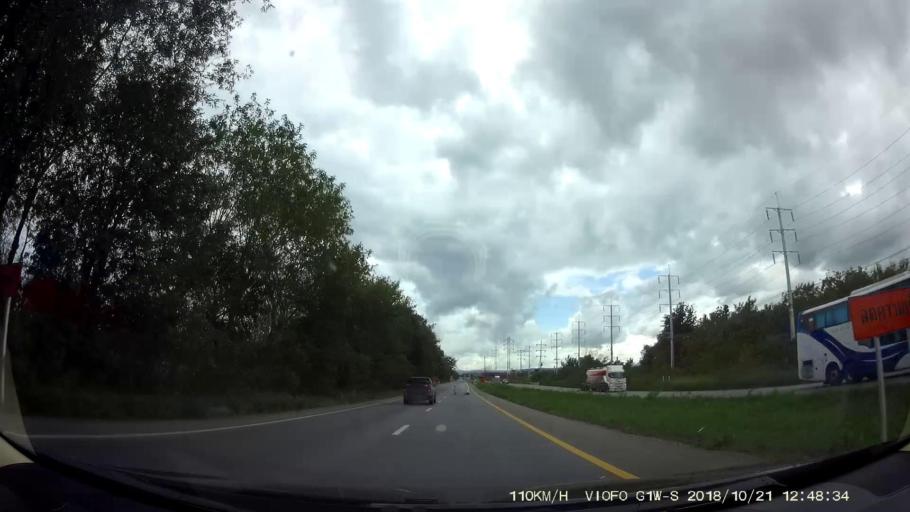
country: TH
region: Nakhon Ratchasima
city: Amphoe Sikhiu
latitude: 14.9103
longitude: 101.6841
